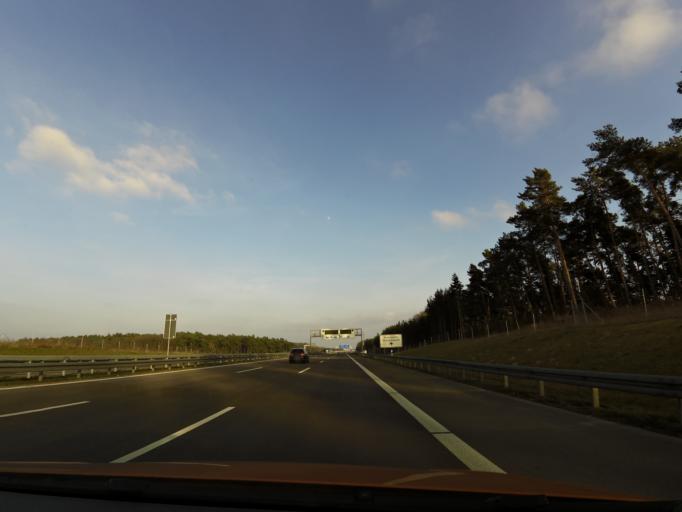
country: DE
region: Brandenburg
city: Kremmen
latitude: 52.7163
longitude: 12.9877
